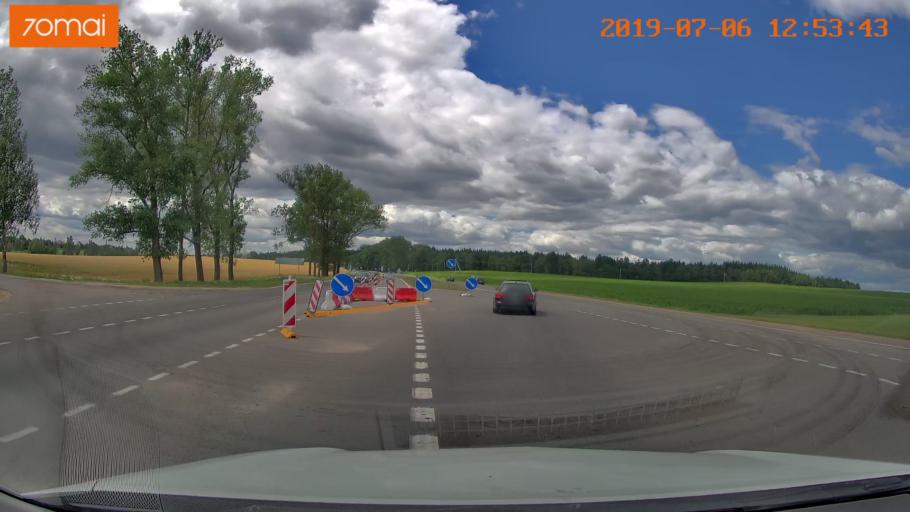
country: BY
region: Minsk
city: Dzyarzhynsk
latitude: 53.7036
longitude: 27.2005
